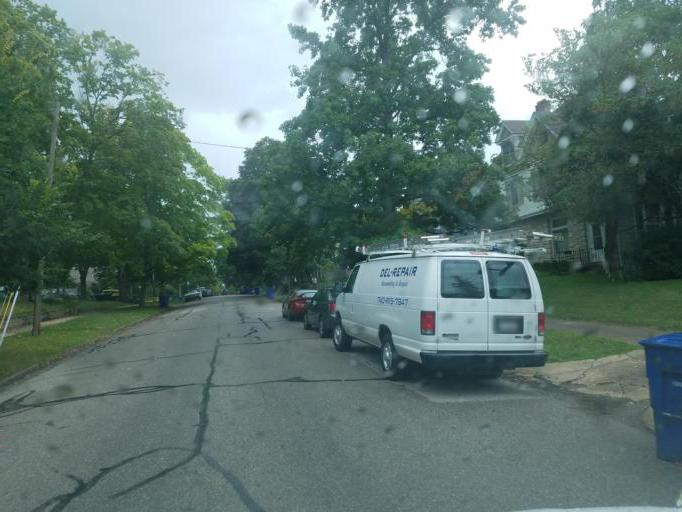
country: US
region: Ohio
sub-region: Delaware County
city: Delaware
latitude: 40.3041
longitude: -83.0691
